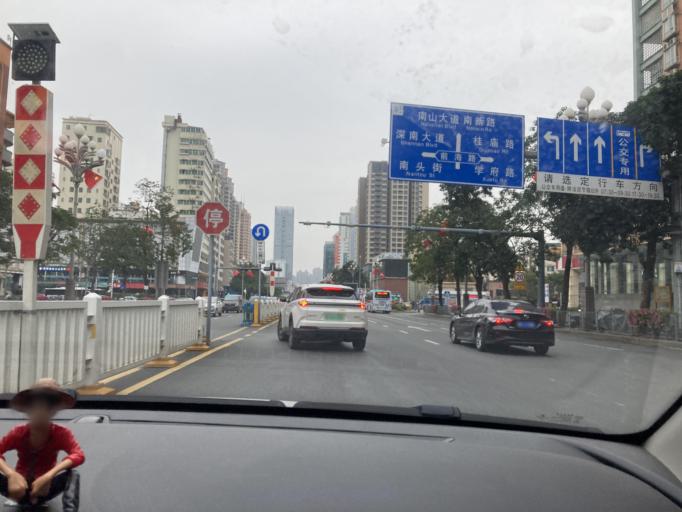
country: CN
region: Guangdong
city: Nantou
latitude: 22.5353
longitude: 113.9092
